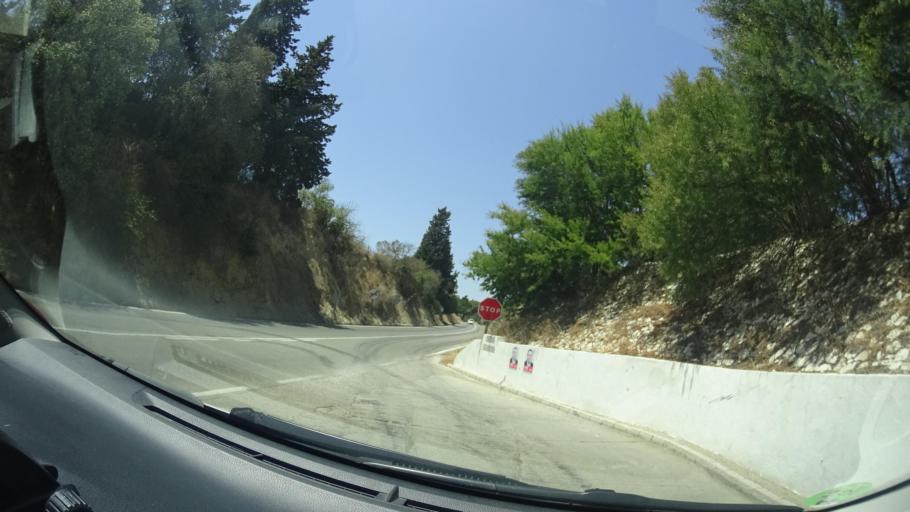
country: ES
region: Andalusia
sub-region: Provincia de Cadiz
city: Jerez de la Frontera
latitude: 36.6604
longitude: -6.1041
